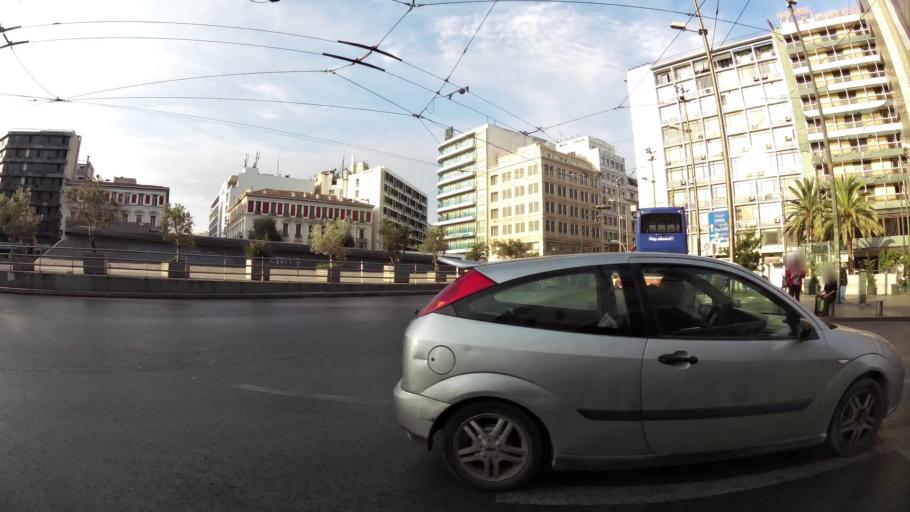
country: GR
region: Attica
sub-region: Nomarchia Athinas
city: Athens
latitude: 37.9845
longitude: 23.7282
